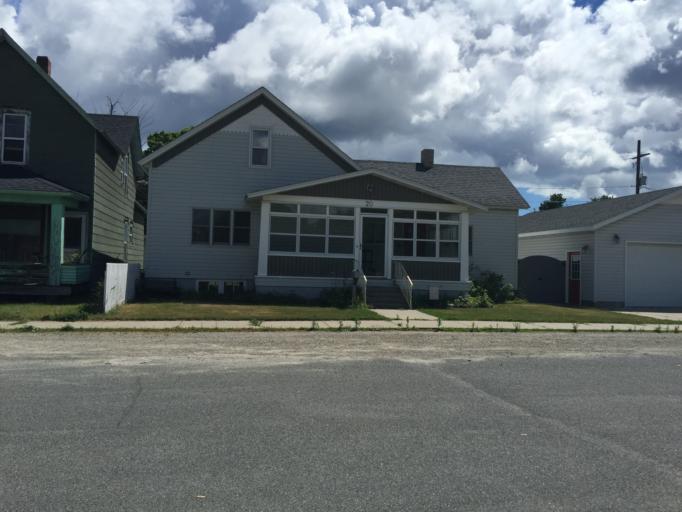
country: US
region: Wisconsin
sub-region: Marinette County
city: Marinette
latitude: 45.0965
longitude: -87.6307
